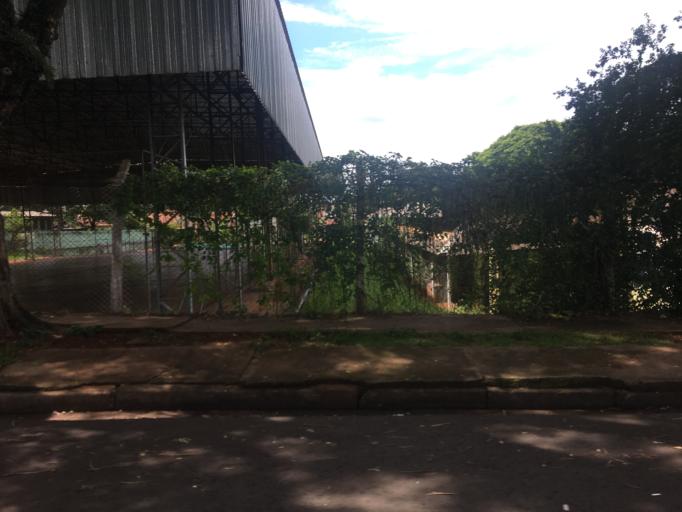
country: BR
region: Parana
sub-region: Maringa
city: Maringa
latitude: -23.4514
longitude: -51.9608
